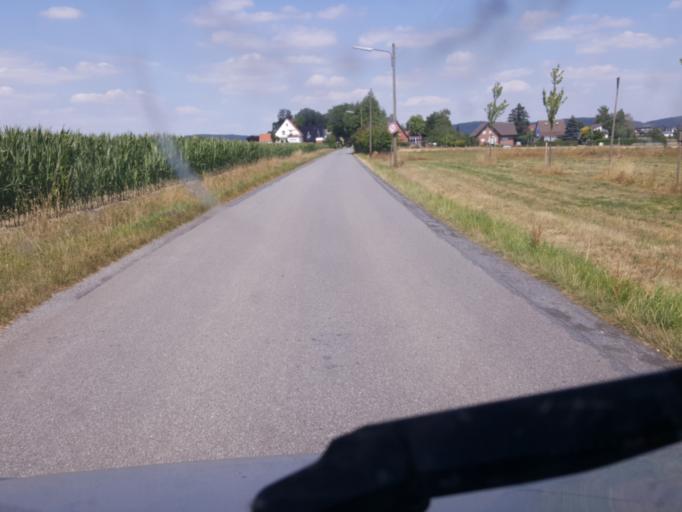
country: DE
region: North Rhine-Westphalia
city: Bad Oeynhausen
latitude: 52.2236
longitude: 8.7624
